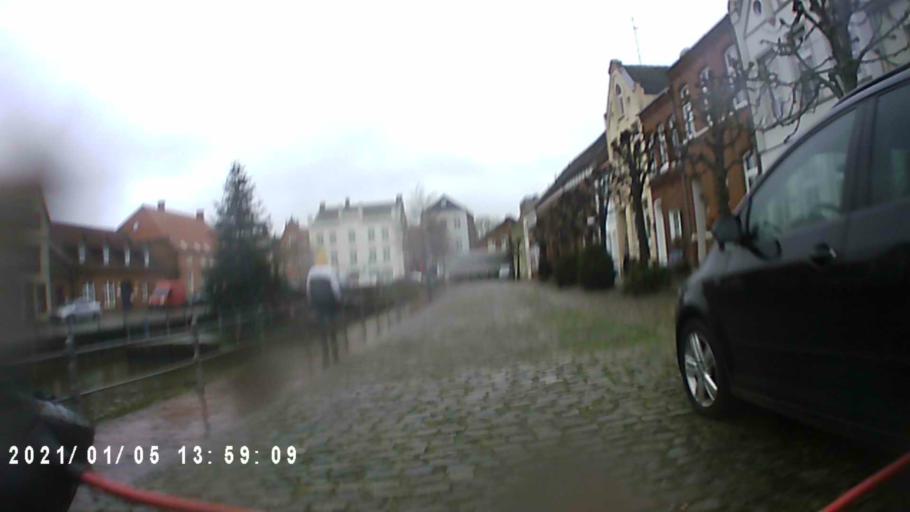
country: DE
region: Lower Saxony
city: Weener
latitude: 53.1693
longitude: 7.3591
